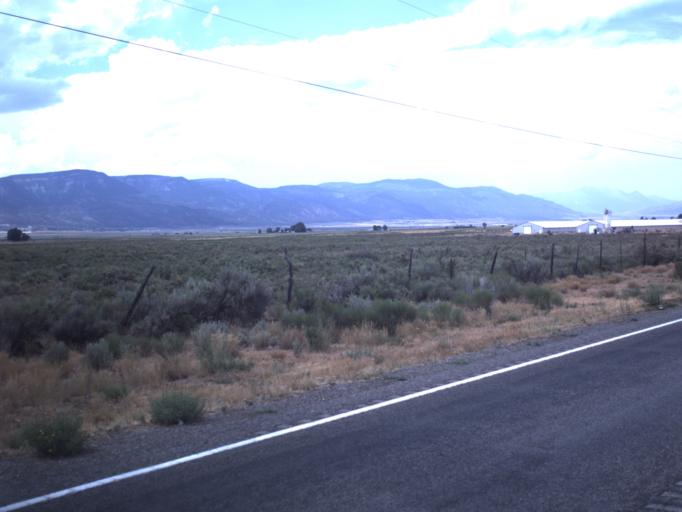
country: US
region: Utah
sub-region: Sanpete County
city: Moroni
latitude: 39.4430
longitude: -111.5624
